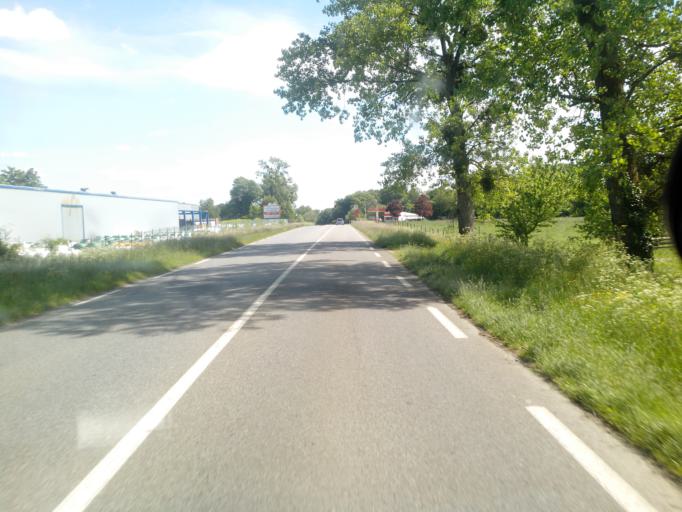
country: FR
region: Haute-Normandie
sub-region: Departement de la Seine-Maritime
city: Tancarville
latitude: 49.4861
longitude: 0.4474
